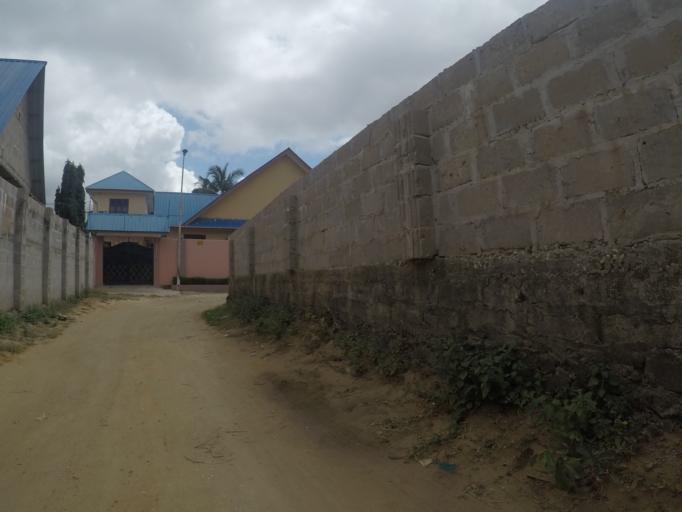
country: TZ
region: Zanzibar Urban/West
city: Zanzibar
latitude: -6.2048
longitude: 39.2302
